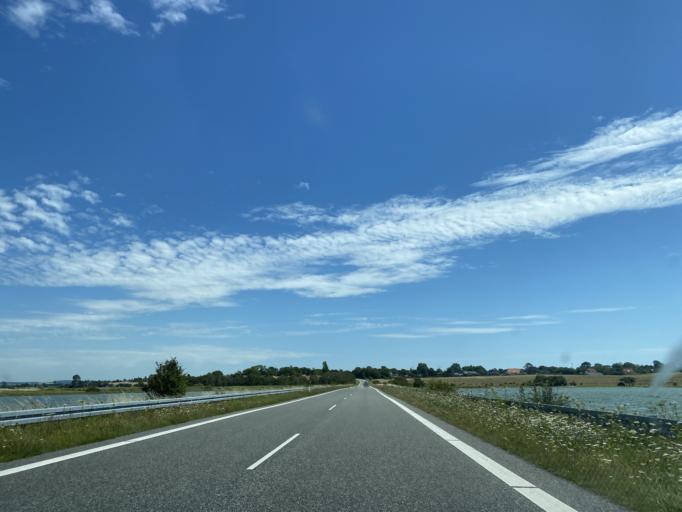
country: DK
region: South Denmark
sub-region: Assens Kommune
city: Harby
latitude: 55.1043
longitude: 10.0880
